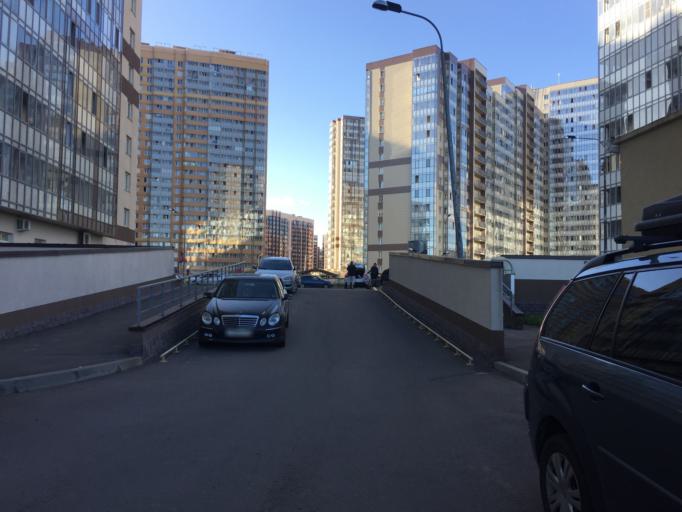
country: RU
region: Leningrad
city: Murino
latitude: 60.0483
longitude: 30.4355
